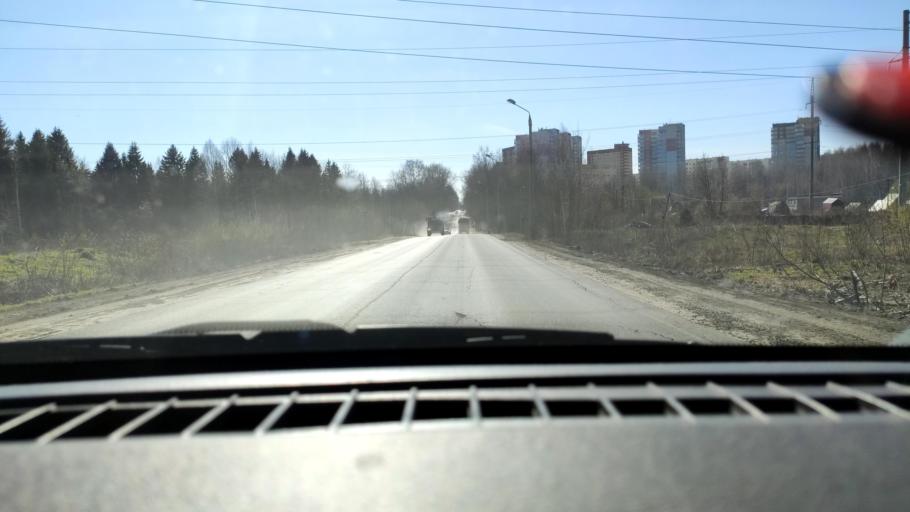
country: RU
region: Perm
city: Polazna
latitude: 58.1353
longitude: 56.4104
